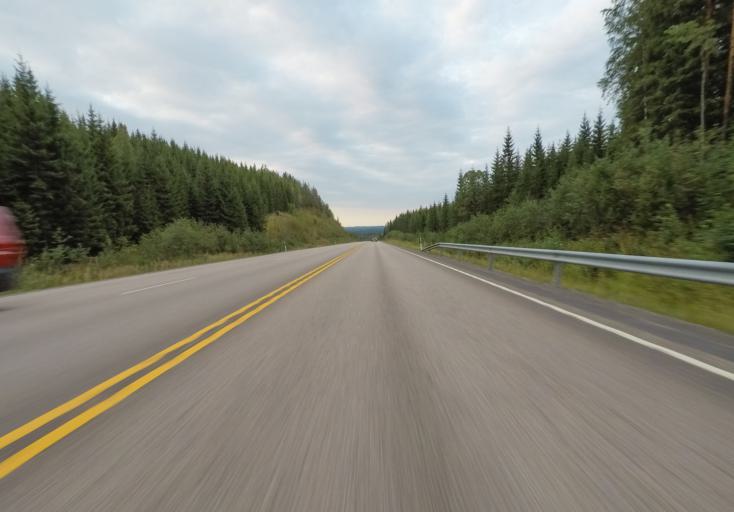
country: FI
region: Central Finland
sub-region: Jyvaeskylae
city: Toivakka
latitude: 62.0468
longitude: 26.0517
